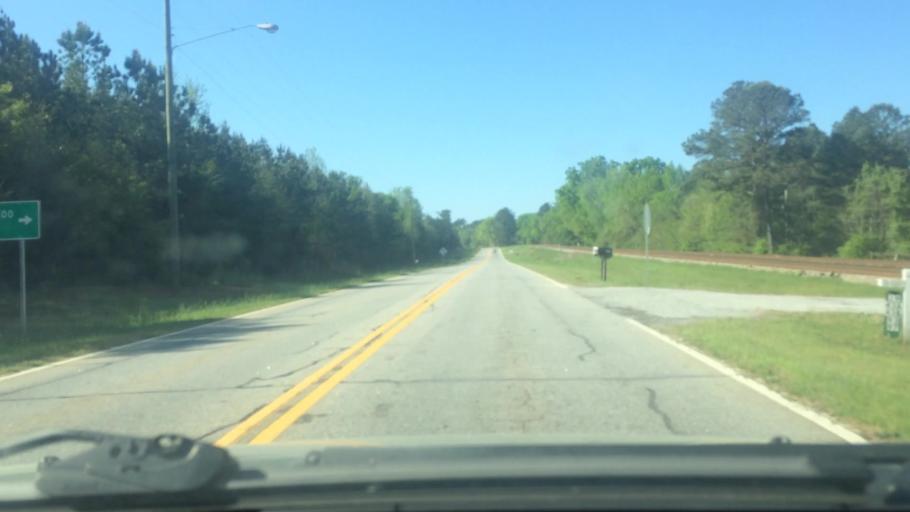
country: US
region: South Carolina
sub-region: Laurens County
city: Laurens
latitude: 34.3636
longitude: -82.0537
